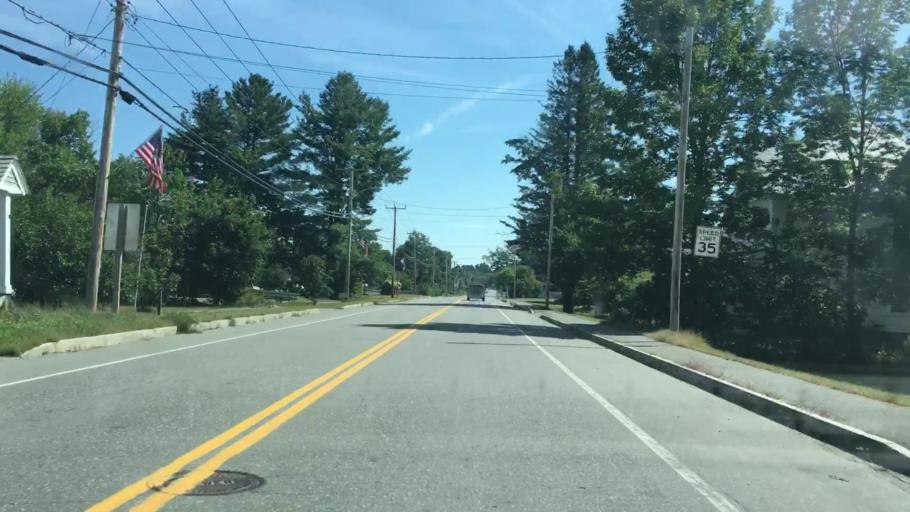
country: US
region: Maine
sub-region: Piscataquis County
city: Milo
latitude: 45.2483
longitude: -68.9796
